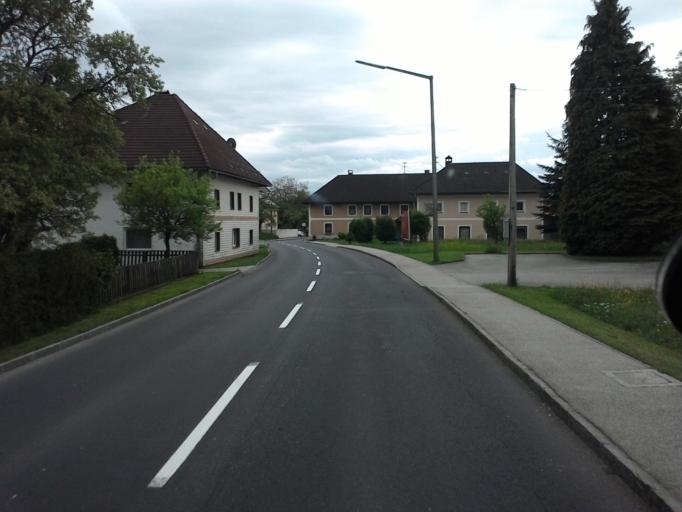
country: AT
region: Upper Austria
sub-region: Wels-Land
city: Sattledt
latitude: 48.0119
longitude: 14.0614
